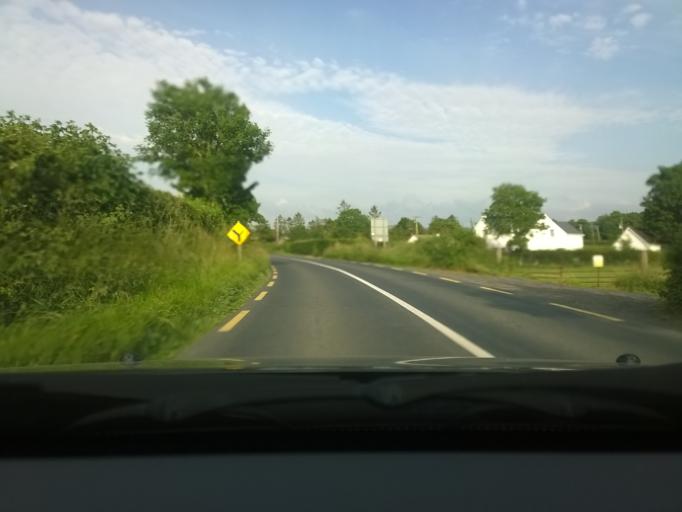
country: IE
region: Leinster
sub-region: Kildare
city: Rathangan
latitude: 53.2143
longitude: -6.9693
